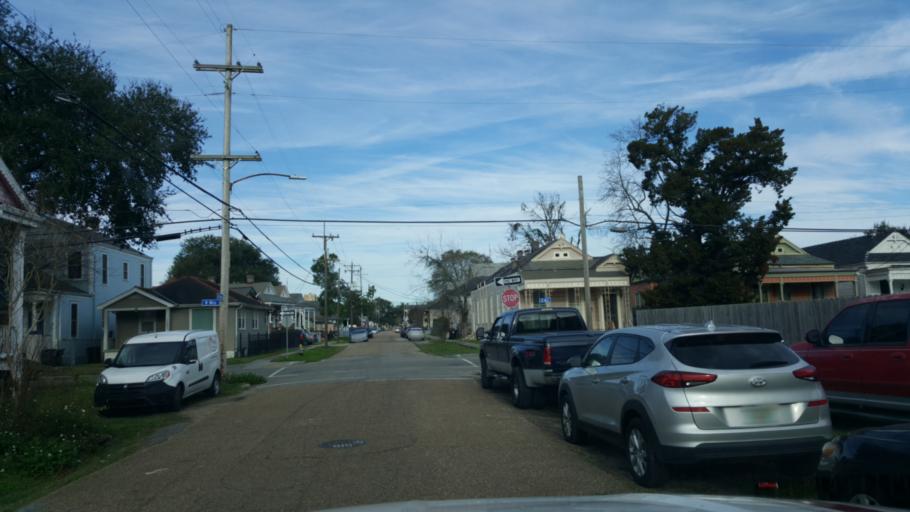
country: US
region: Louisiana
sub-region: Orleans Parish
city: New Orleans
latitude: 29.9745
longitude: -90.0721
